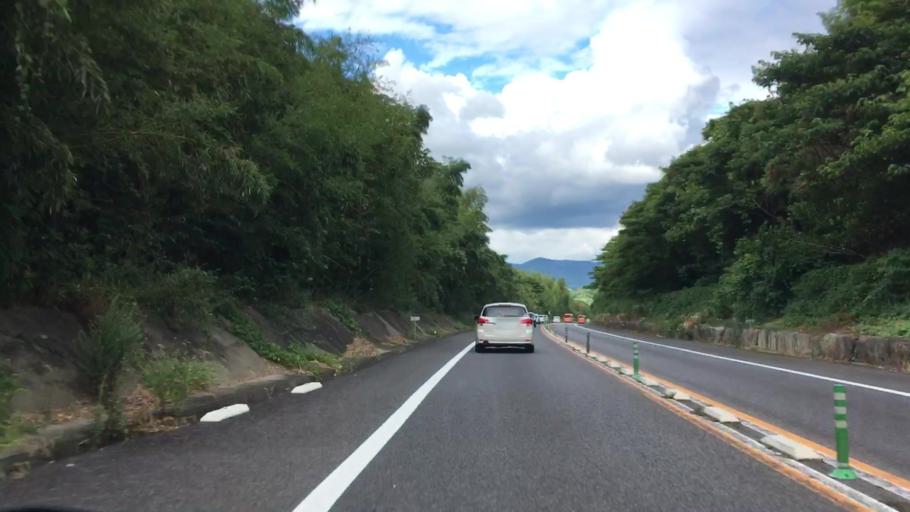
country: JP
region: Saga Prefecture
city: Karatsu
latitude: 33.4247
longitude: 130.0370
